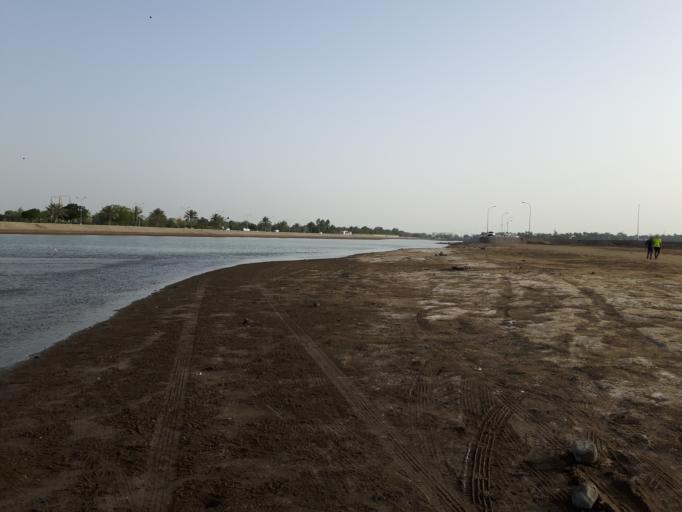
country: OM
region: Al Batinah
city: Al Sohar
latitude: 24.4091
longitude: 56.7153
